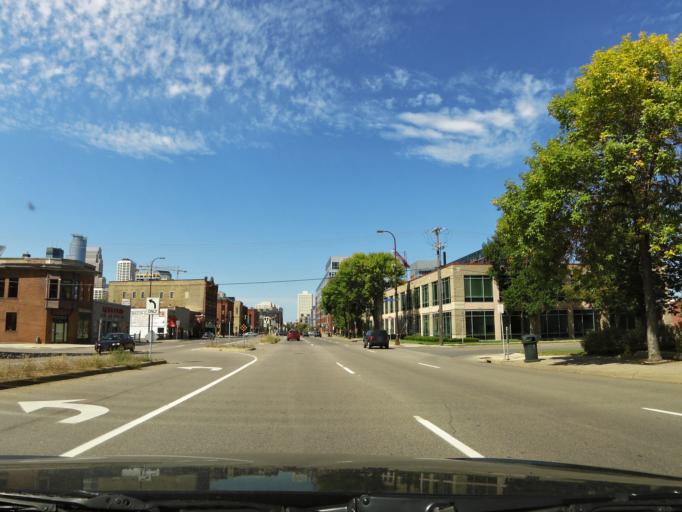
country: US
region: Minnesota
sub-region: Hennepin County
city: Minneapolis
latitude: 44.9747
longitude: -93.2513
